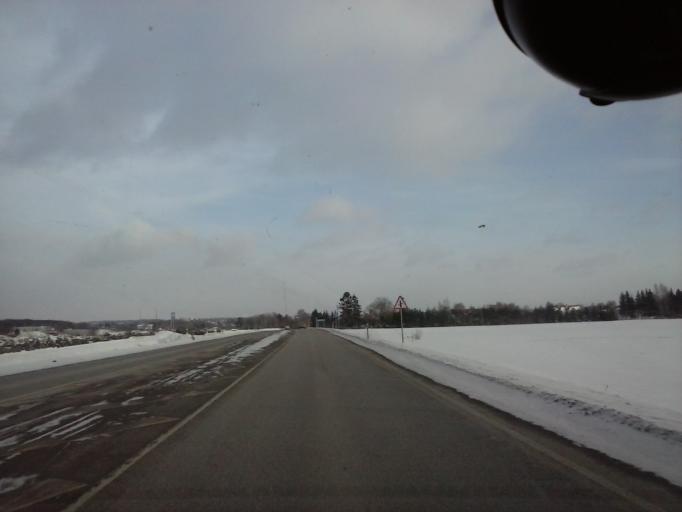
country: EE
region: Tartu
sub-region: Noo vald
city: Noo
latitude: 58.3539
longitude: 26.5953
